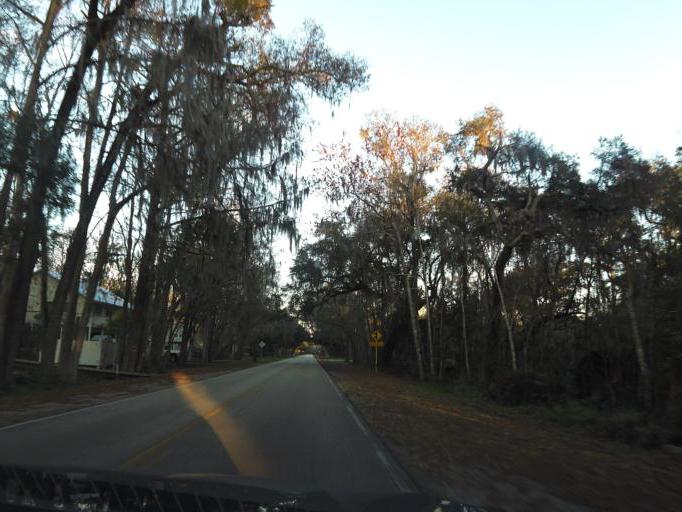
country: US
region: Florida
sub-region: Clay County
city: Green Cove Springs
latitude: 29.9259
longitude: -81.5865
